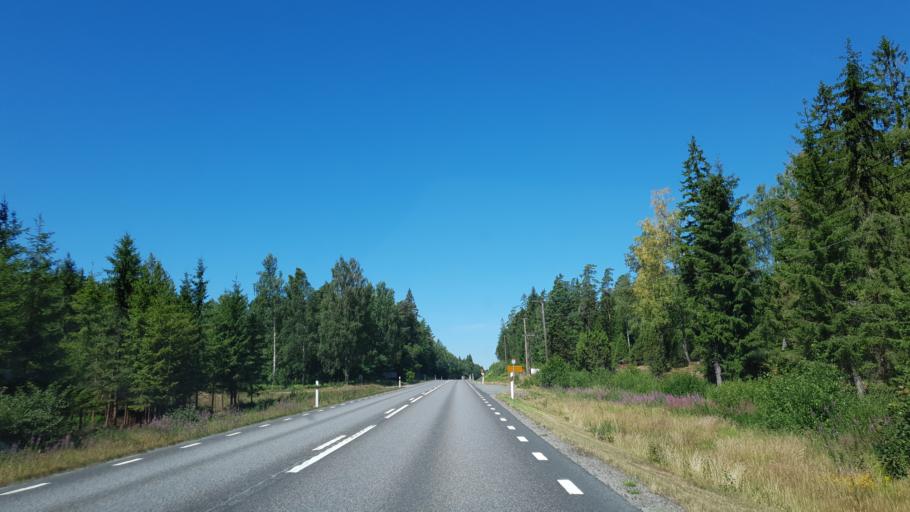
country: SE
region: Joenkoeping
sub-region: Varnamo Kommun
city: Bor
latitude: 57.0552
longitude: 14.2115
